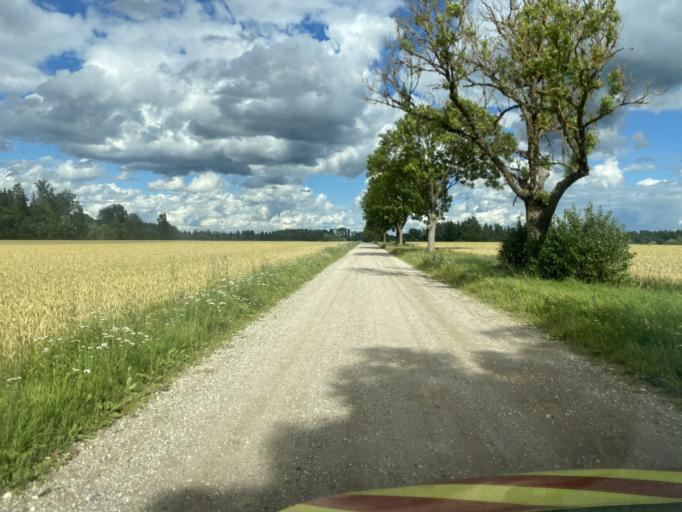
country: EE
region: Viljandimaa
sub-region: Viiratsi vald
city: Viiratsi
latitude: 58.3984
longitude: 25.7747
